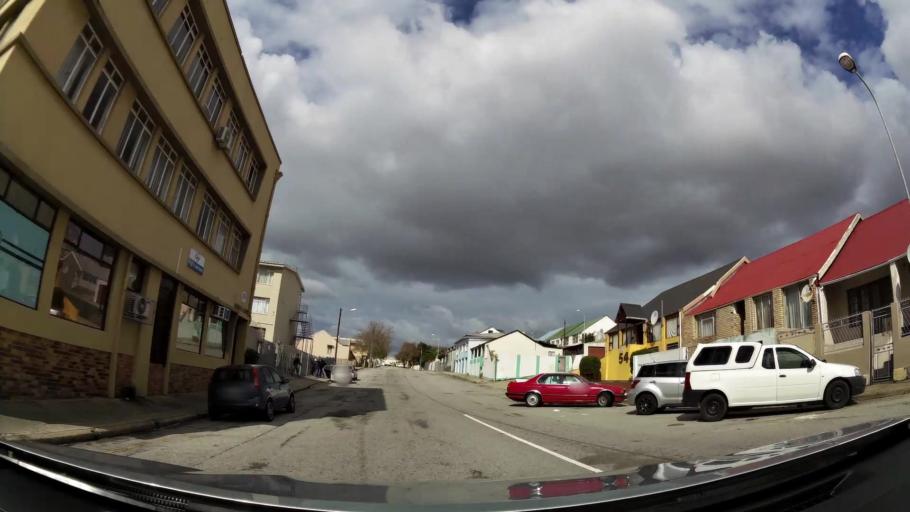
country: ZA
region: Eastern Cape
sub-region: Nelson Mandela Bay Metropolitan Municipality
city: Port Elizabeth
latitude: -33.9515
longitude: 25.6068
